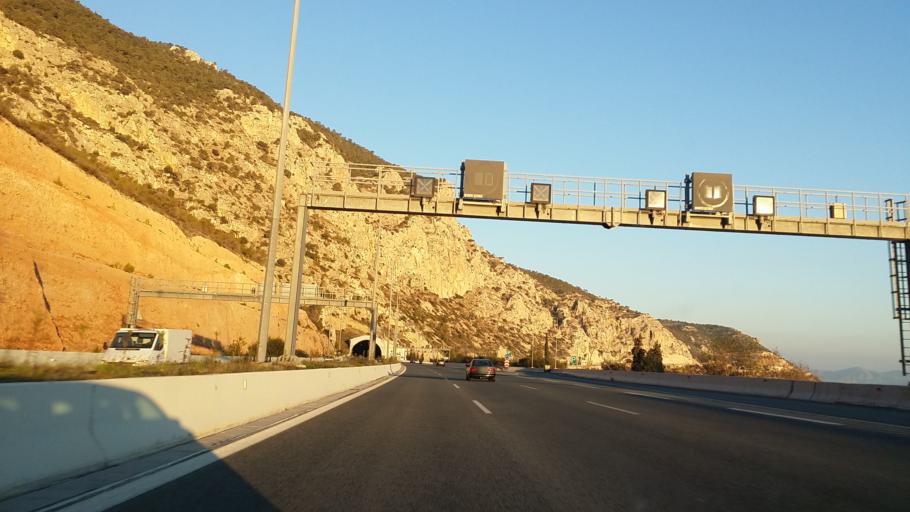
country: GR
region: Attica
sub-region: Nomarchia Dytikis Attikis
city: Kineta
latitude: 37.9782
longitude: 23.2616
